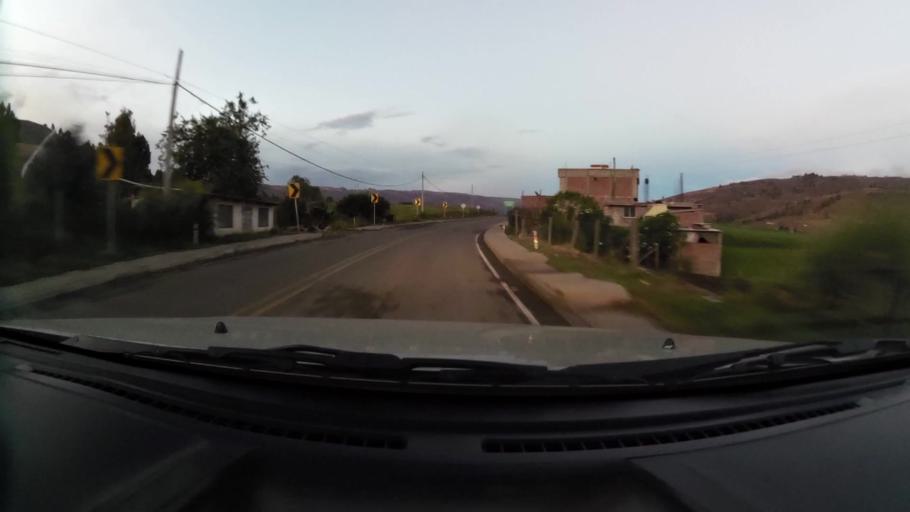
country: EC
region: Chimborazo
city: Riobamba
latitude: -1.9166
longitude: -78.6994
